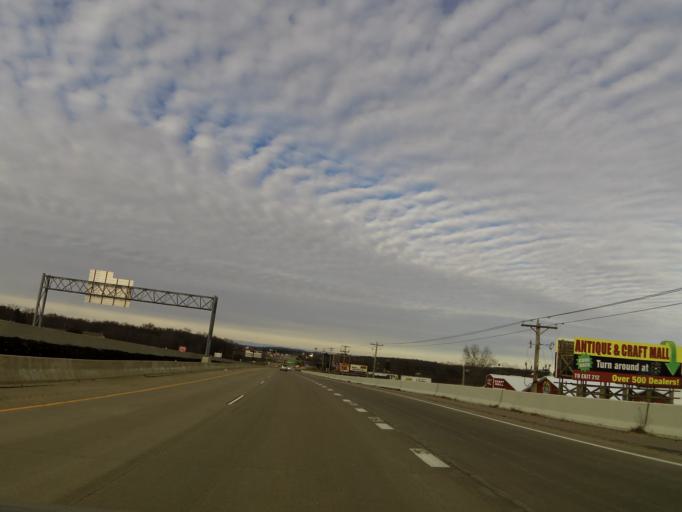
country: US
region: Wisconsin
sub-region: Sauk County
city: Lake Delton
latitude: 43.5616
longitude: -89.7781
